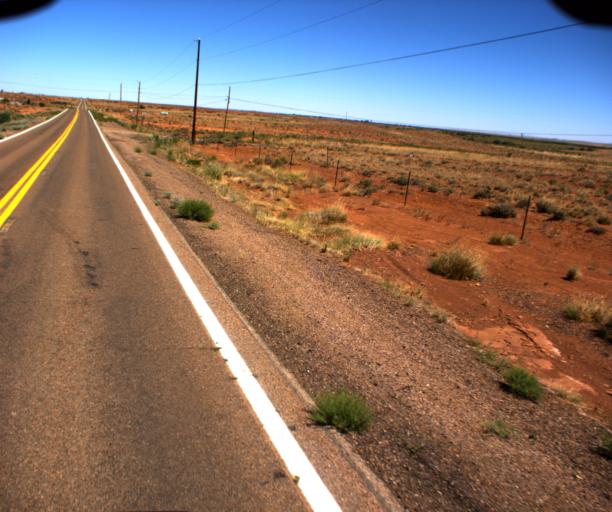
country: US
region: Arizona
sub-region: Navajo County
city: Winslow
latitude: 34.9794
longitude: -110.6576
